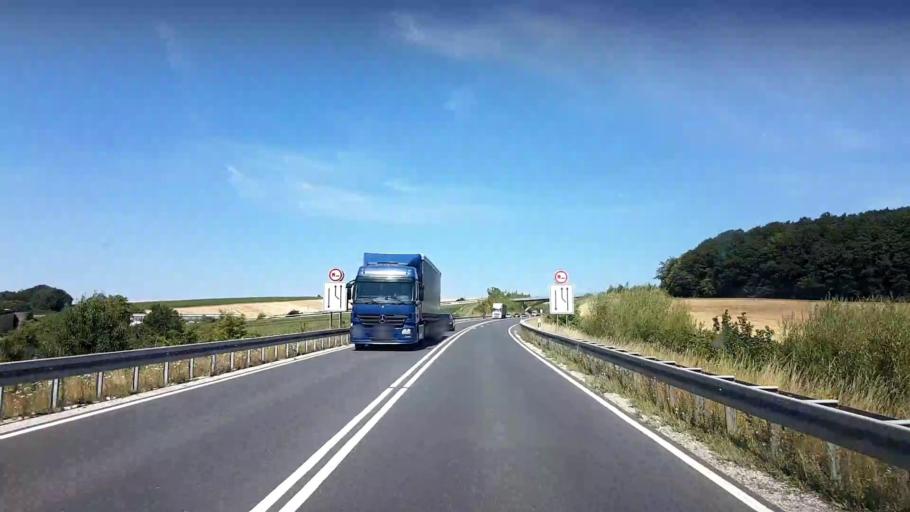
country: DE
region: Bavaria
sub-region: Upper Franconia
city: Untersiemau
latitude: 50.1666
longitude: 10.9982
